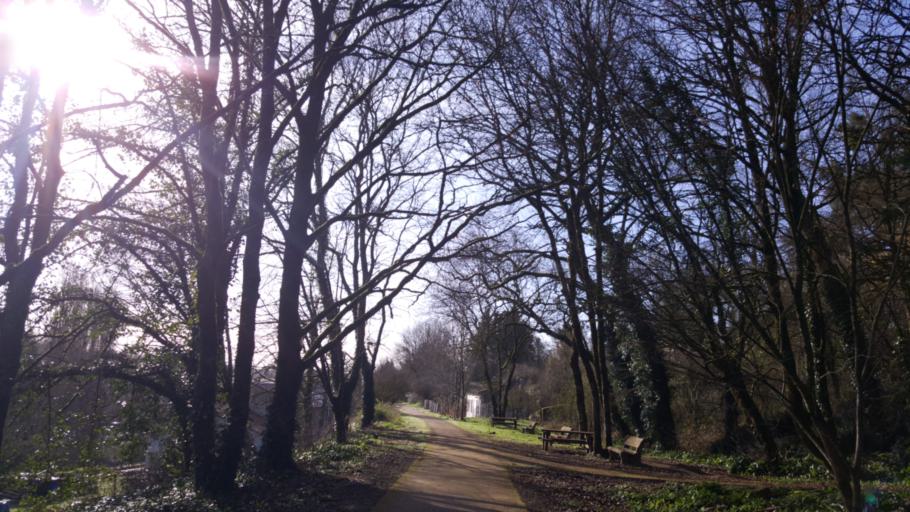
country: FR
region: Poitou-Charentes
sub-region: Departement des Deux-Sevres
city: Melle
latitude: 46.2226
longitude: -0.1517
